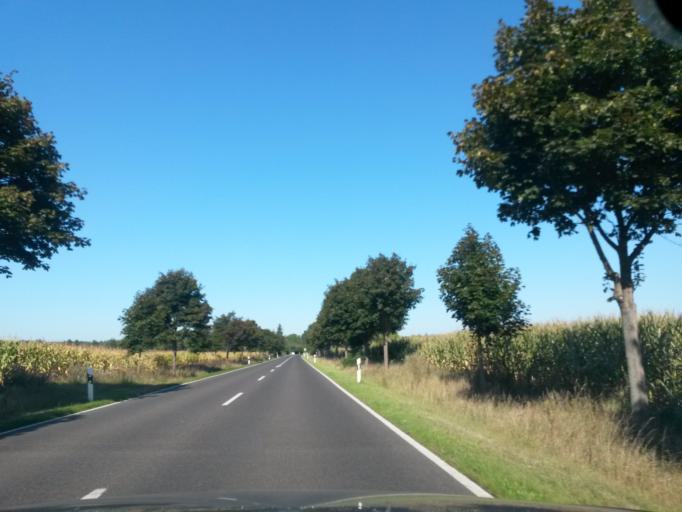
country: DE
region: Brandenburg
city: Templin
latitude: 53.1464
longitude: 13.4580
